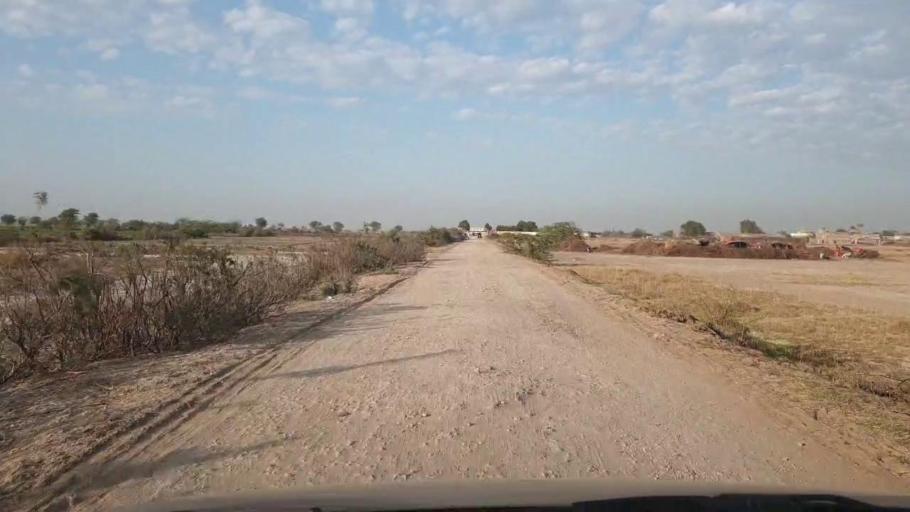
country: PK
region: Sindh
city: Sakrand
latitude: 26.0276
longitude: 68.3838
